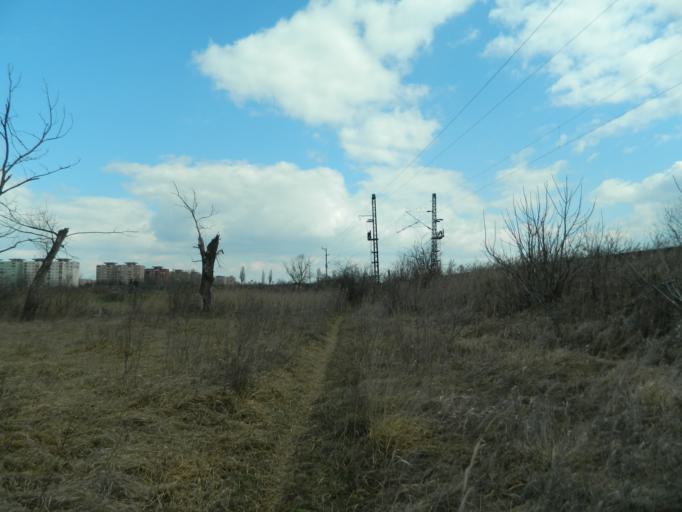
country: HU
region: Fejer
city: Szekesfehervar
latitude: 47.1760
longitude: 18.4025
